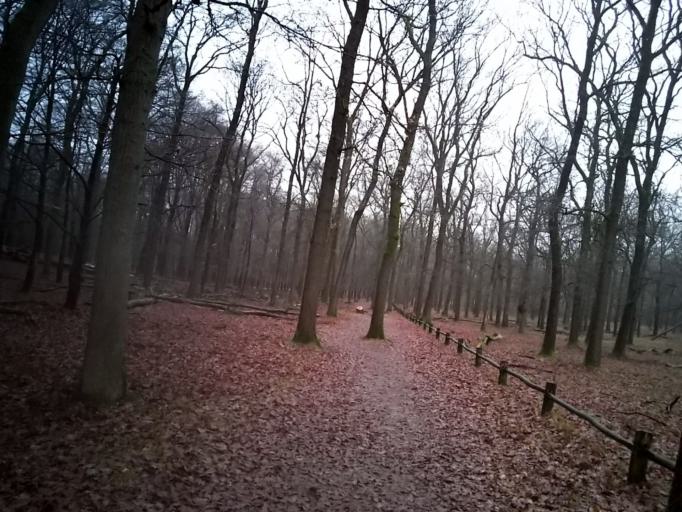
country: NL
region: Gelderland
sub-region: Gemeente Apeldoorn
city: Uddel
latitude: 52.2318
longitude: 5.8407
